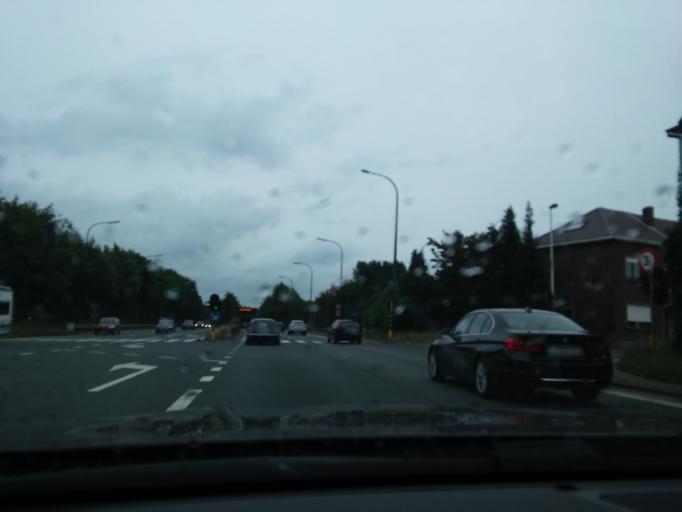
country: BE
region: Flanders
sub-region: Provincie Vlaams-Brabant
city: Halle
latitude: 50.7234
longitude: 4.2541
